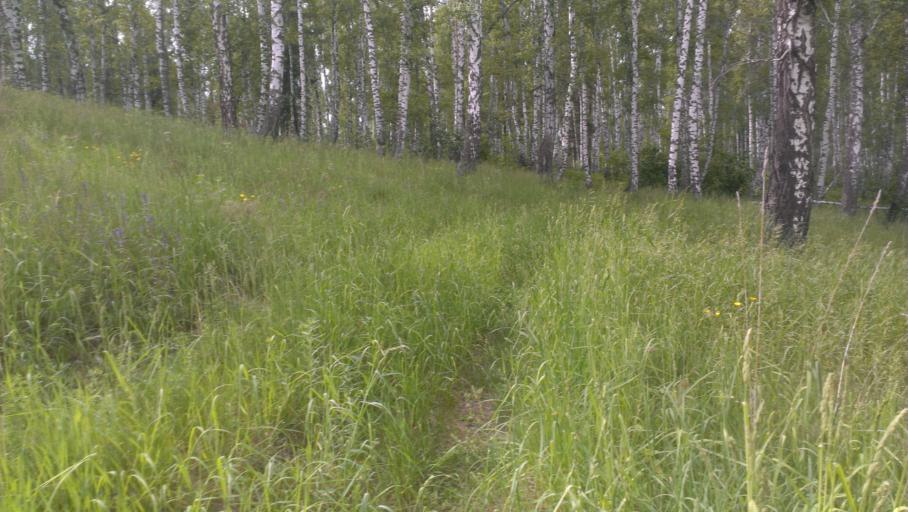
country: RU
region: Altai Krai
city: Sannikovo
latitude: 53.3396
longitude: 84.0579
